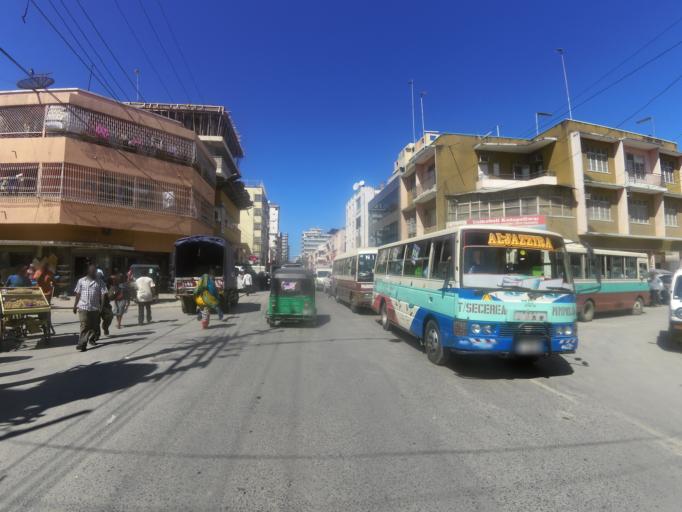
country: TZ
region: Dar es Salaam
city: Dar es Salaam
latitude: -6.8227
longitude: 39.2762
